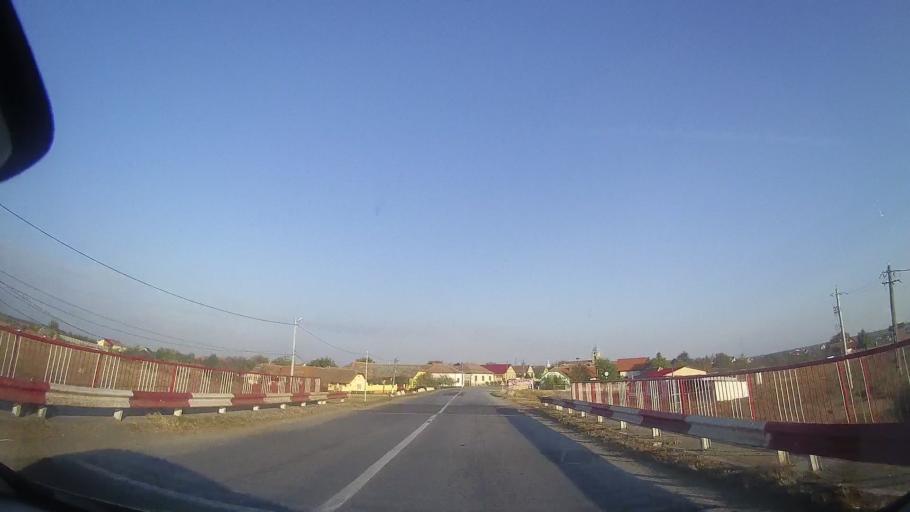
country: RO
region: Timis
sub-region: Comuna Pischia
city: Pischia
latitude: 45.8992
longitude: 21.3415
